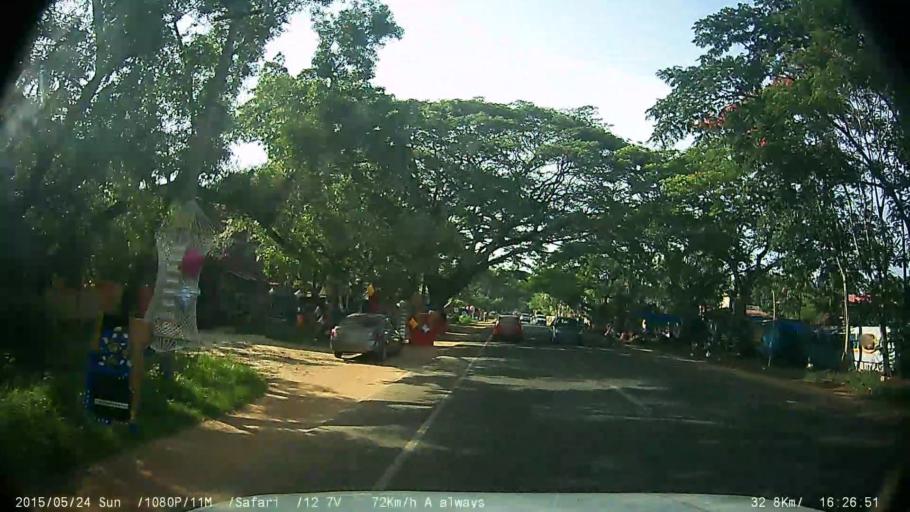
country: IN
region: Kerala
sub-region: Alappuzha
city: Alleppey
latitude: 9.5226
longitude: 76.3276
